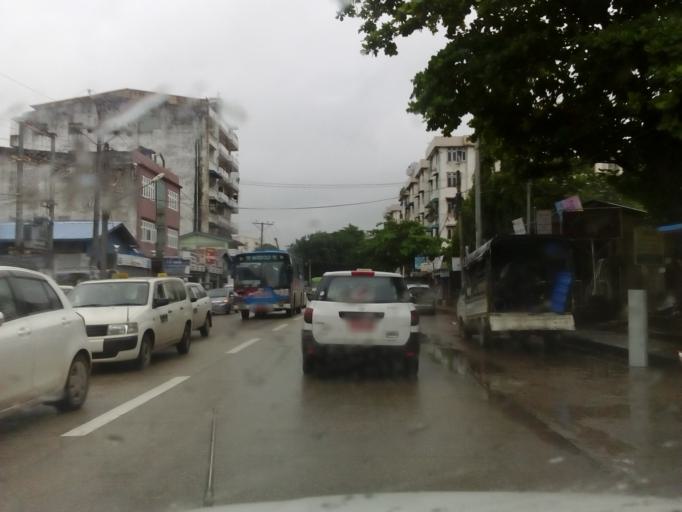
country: MM
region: Yangon
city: Yangon
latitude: 16.8136
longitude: 96.1739
